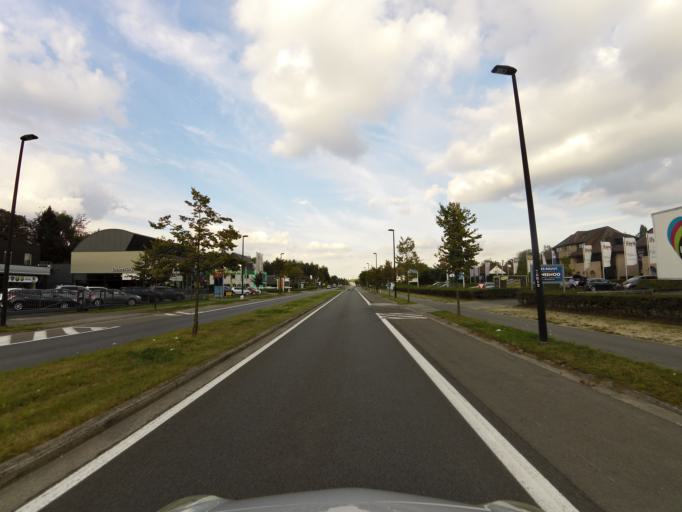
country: BE
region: Flanders
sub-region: Provincie Oost-Vlaanderen
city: Sint-Martens-Latem
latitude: 51.0074
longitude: 3.6295
